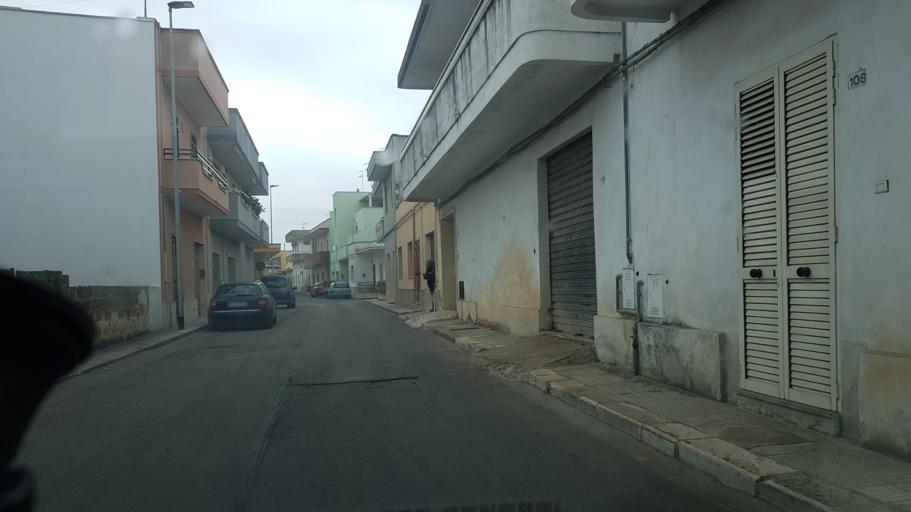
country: IT
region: Apulia
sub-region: Provincia di Lecce
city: Leverano
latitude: 40.2859
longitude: 17.9922
